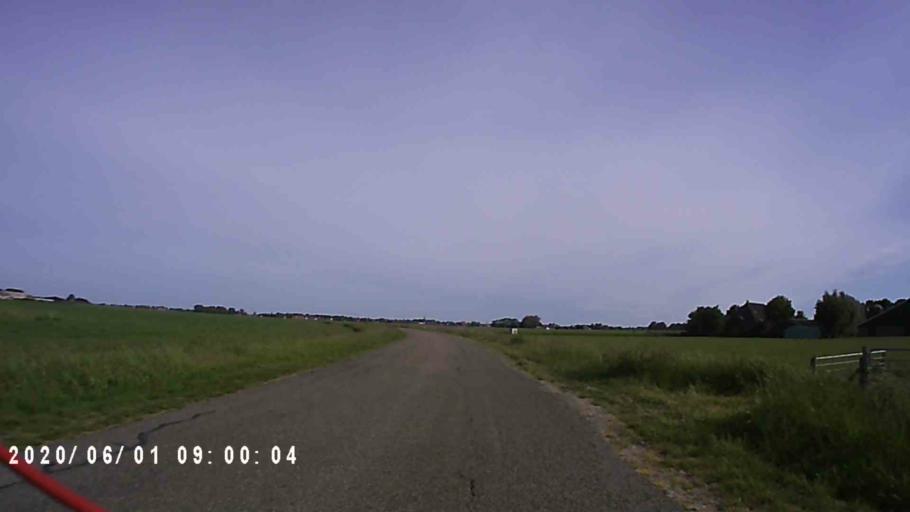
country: NL
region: Friesland
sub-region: Gemeente Ferwerderadiel
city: Hallum
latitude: 53.2857
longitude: 5.7976
